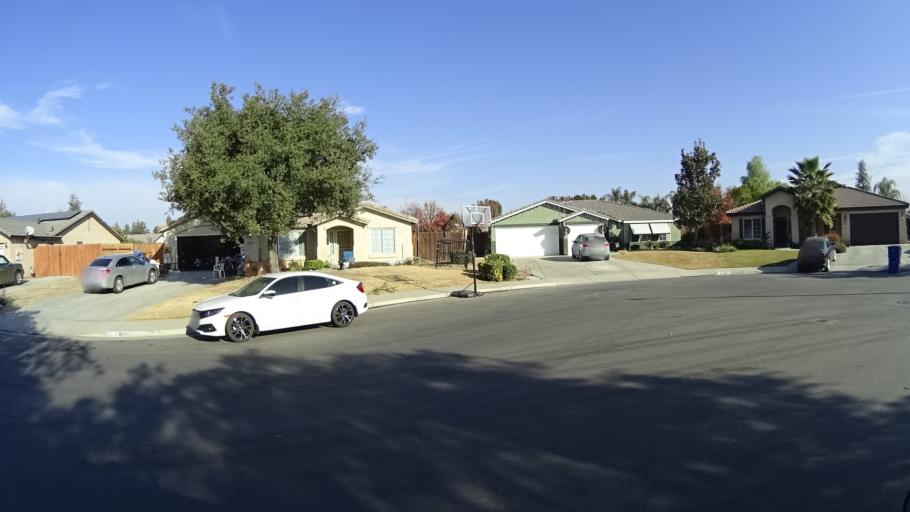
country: US
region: California
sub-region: Kern County
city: Oildale
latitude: 35.4071
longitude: -119.0637
